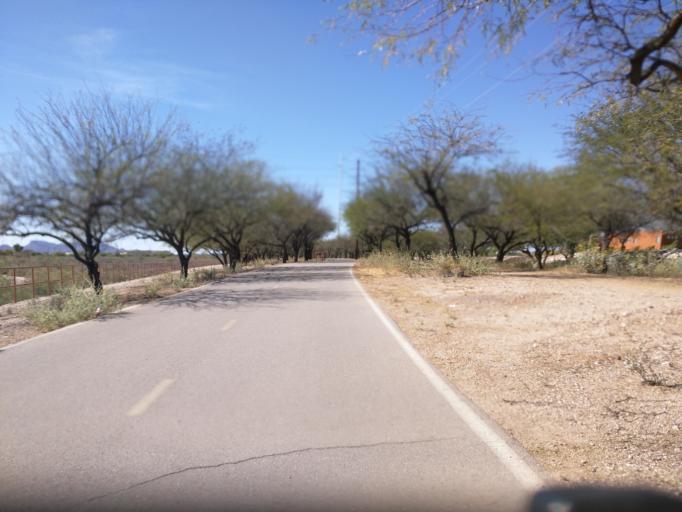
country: US
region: Arizona
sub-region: Pima County
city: Flowing Wells
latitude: 32.2982
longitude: -111.0035
